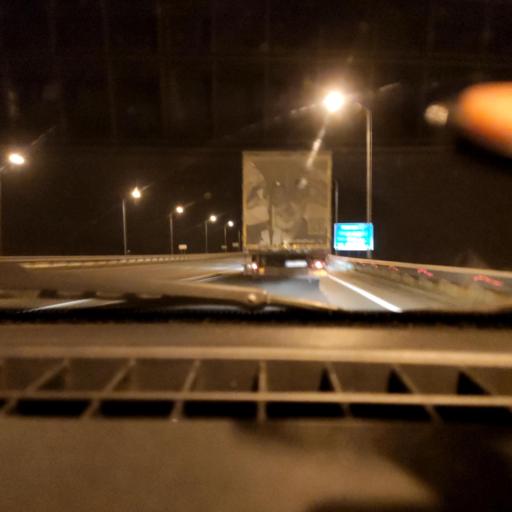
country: RU
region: Bashkortostan
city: Mikhaylovka
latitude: 54.8757
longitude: 55.7107
